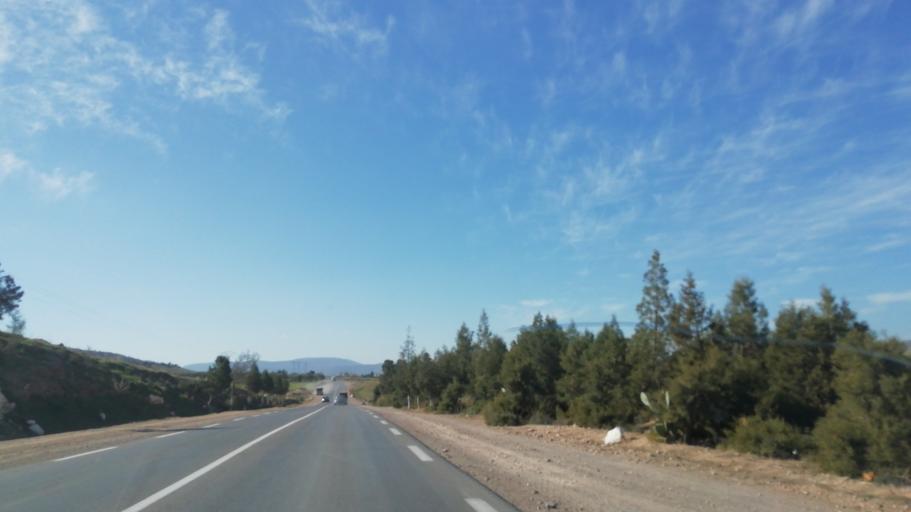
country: DZ
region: Tlemcen
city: Ouled Mimoun
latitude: 34.8929
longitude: -1.0649
